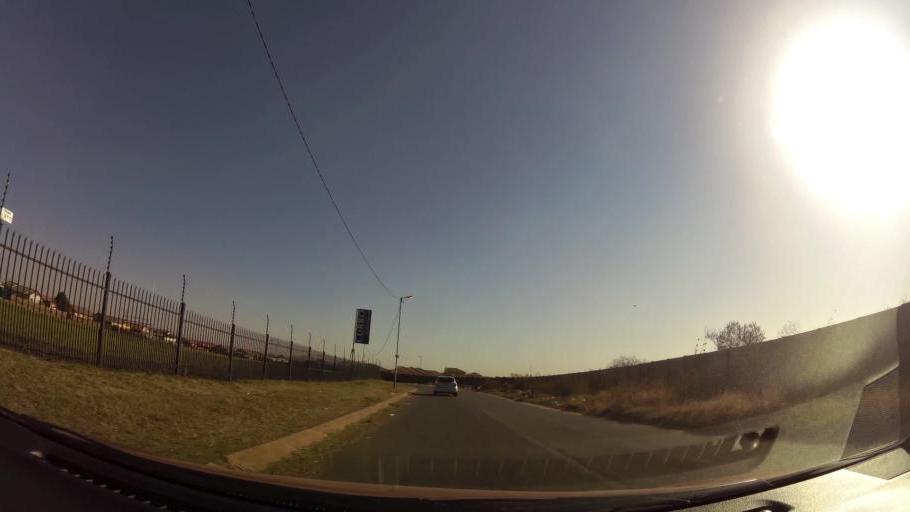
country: ZA
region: Gauteng
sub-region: City of Tshwane Metropolitan Municipality
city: Mabopane
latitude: -25.5723
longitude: 28.0918
